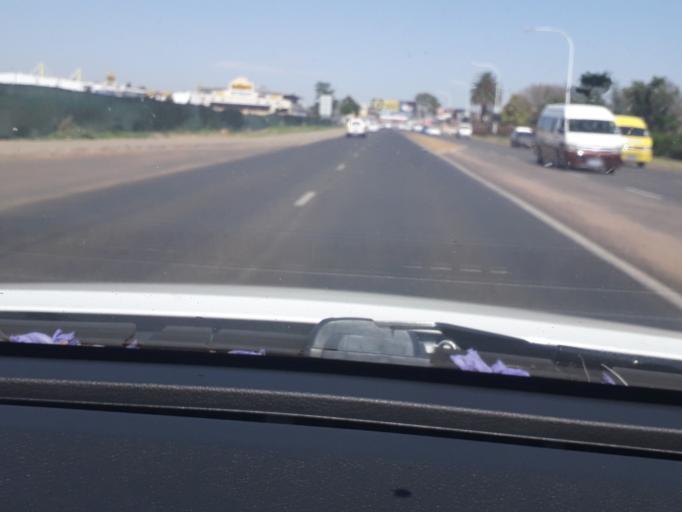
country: ZA
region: Gauteng
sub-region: Ekurhuleni Metropolitan Municipality
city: Boksburg
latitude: -26.1791
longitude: 28.2635
